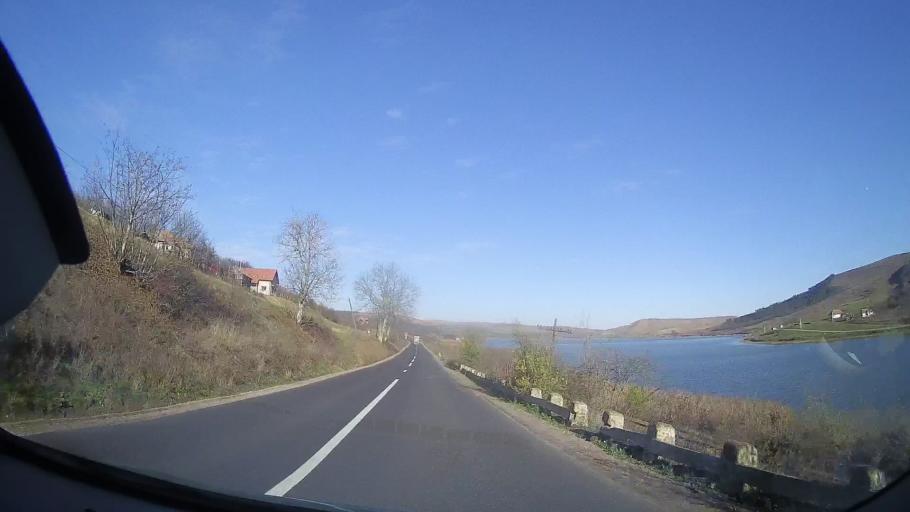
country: RO
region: Mures
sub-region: Comuna Zau De Campie
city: Zau de Campie
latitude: 46.6214
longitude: 24.1316
